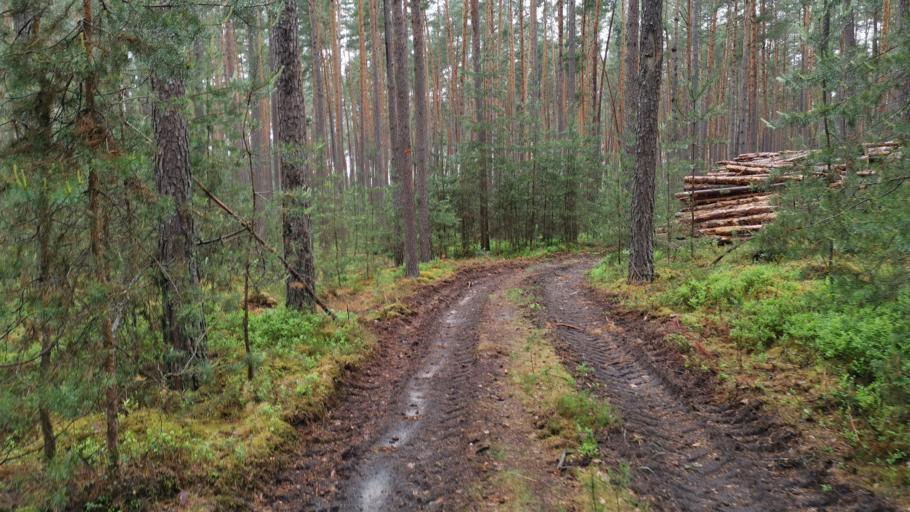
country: DE
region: Bavaria
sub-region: Regierungsbezirk Mittelfranken
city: Roth
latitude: 49.2559
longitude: 11.1164
